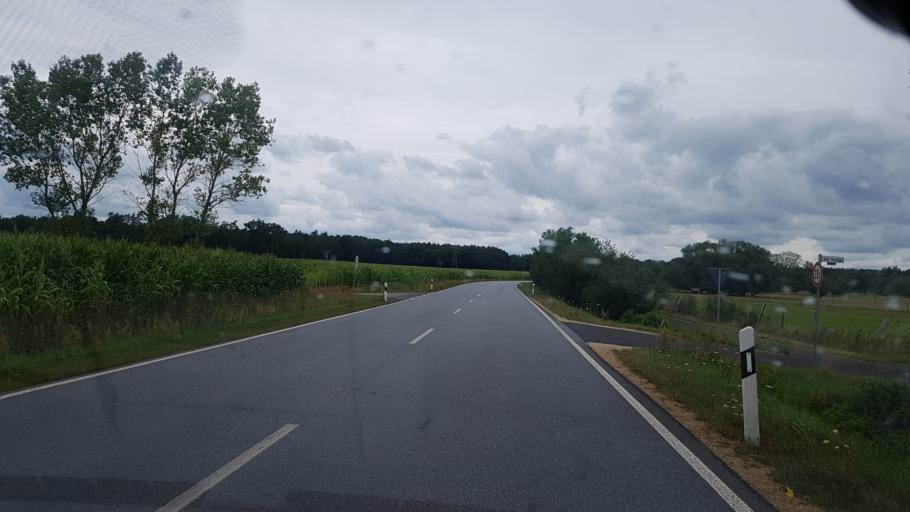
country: DE
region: Saxony
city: Niesky
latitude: 51.2611
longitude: 14.8093
